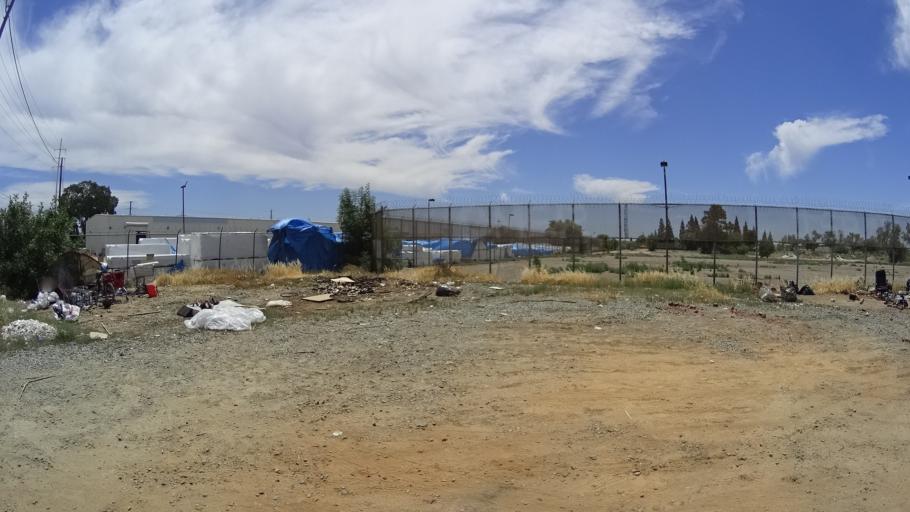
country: US
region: California
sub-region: Sacramento County
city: Rosemont
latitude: 38.5478
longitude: -121.4111
